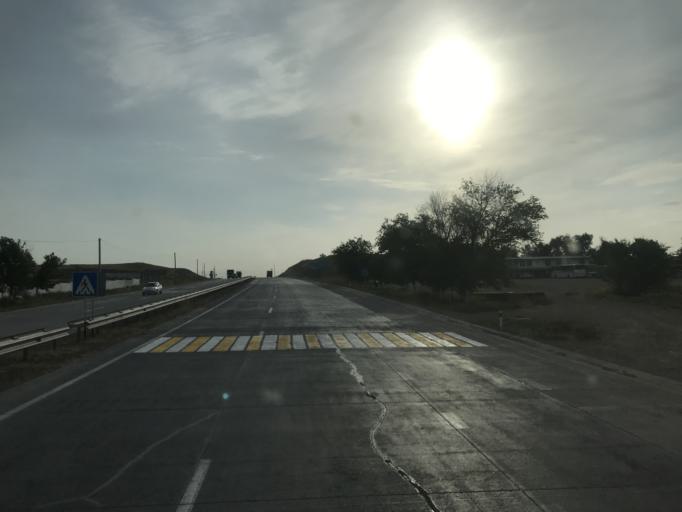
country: UZ
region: Toshkent
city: Salor
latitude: 41.5052
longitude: 69.3717
